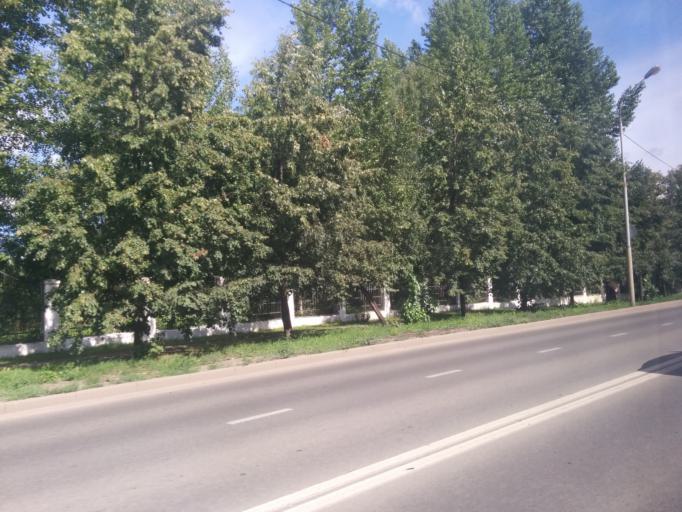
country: RU
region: Tatarstan
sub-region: Gorod Kazan'
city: Kazan
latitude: 55.7965
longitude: 49.1944
